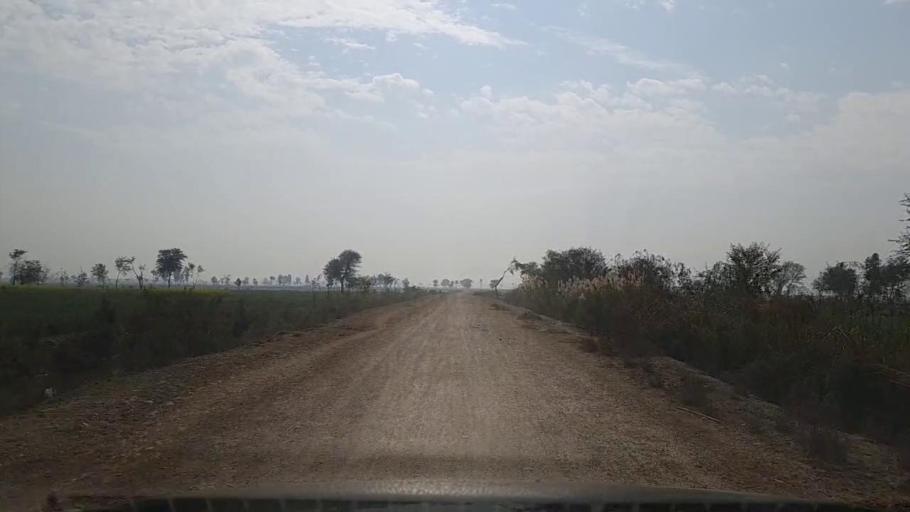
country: PK
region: Sindh
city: Daur
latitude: 26.3829
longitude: 68.3824
